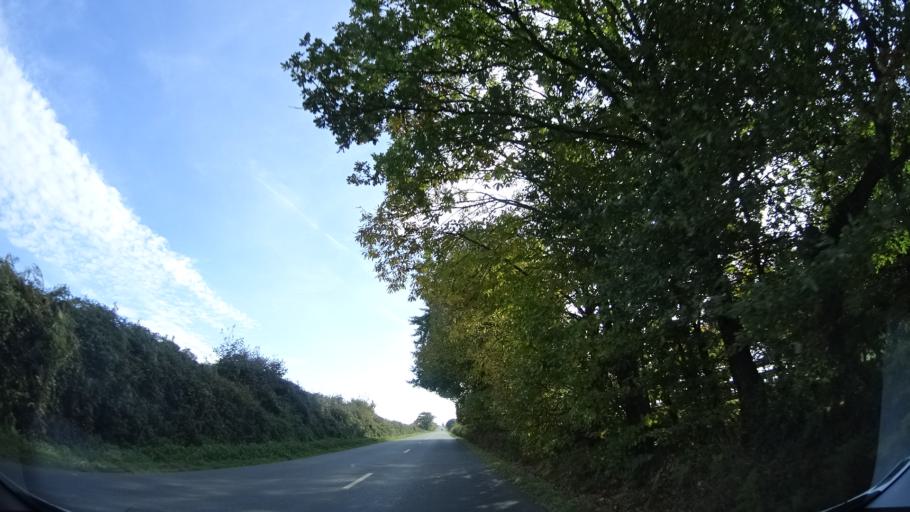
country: FR
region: Brittany
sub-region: Departement d'Ille-et-Vilaine
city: Bedee
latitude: 48.2055
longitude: -1.9409
